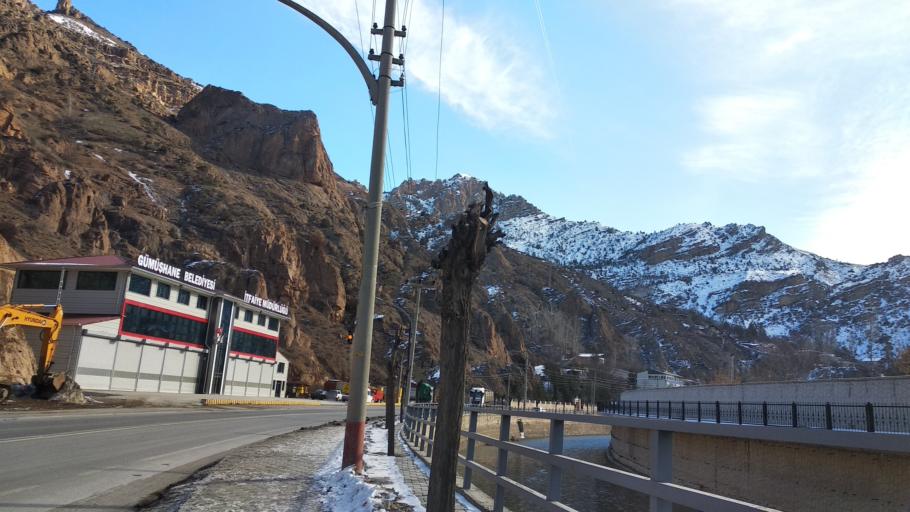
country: TR
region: Gumushane
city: Gumushkhane
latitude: 40.4474
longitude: 39.4996
